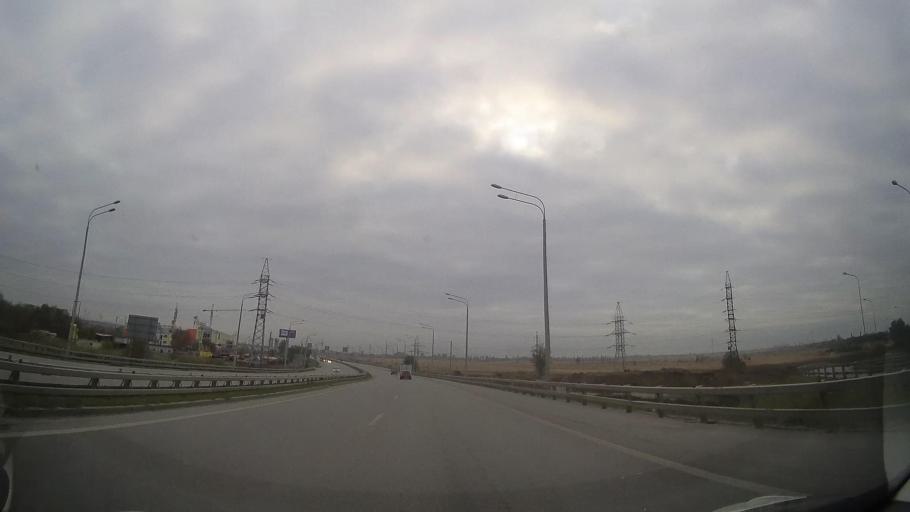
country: RU
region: Rostov
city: Rostov-na-Donu
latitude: 47.2030
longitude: 39.7119
